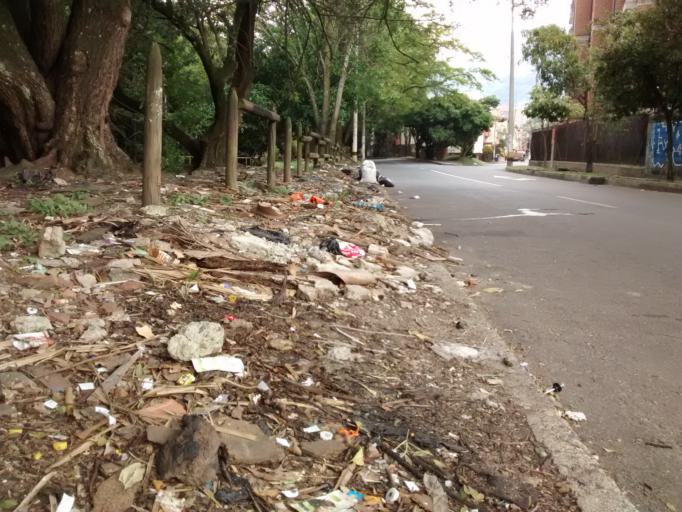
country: CO
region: Antioquia
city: Medellin
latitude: 6.2246
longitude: -75.5829
